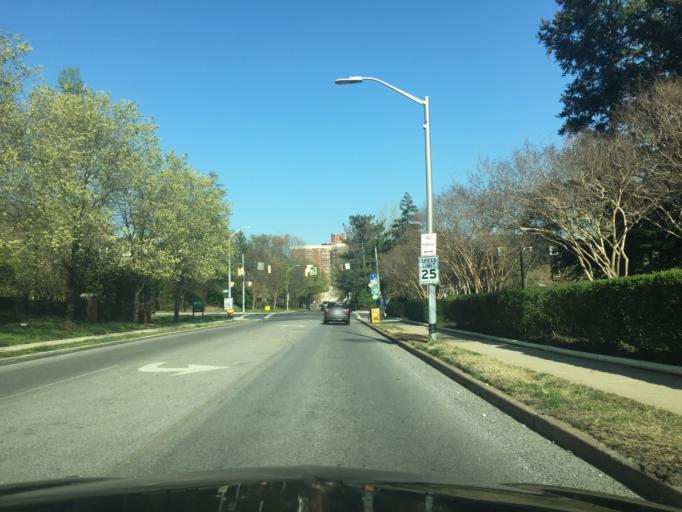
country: US
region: Maryland
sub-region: City of Baltimore
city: Baltimore
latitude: 39.3371
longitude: -76.6294
